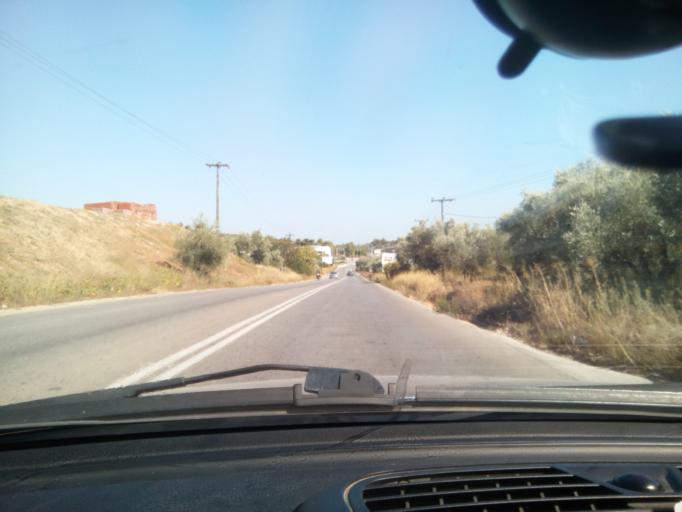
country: GR
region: Central Greece
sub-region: Nomos Evvoias
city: Vasilikon
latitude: 38.4181
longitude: 23.6899
